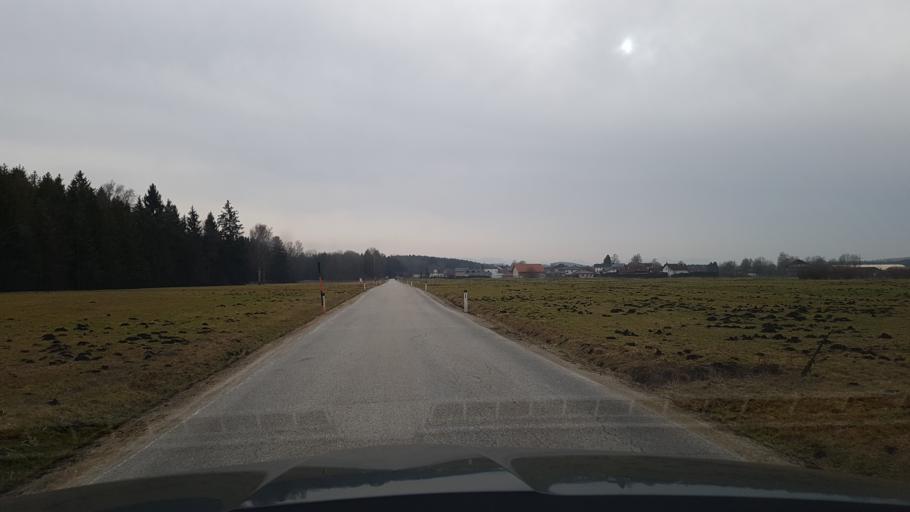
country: AT
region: Salzburg
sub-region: Politischer Bezirk Salzburg-Umgebung
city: Lamprechtshausen
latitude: 48.0503
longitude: 12.9543
